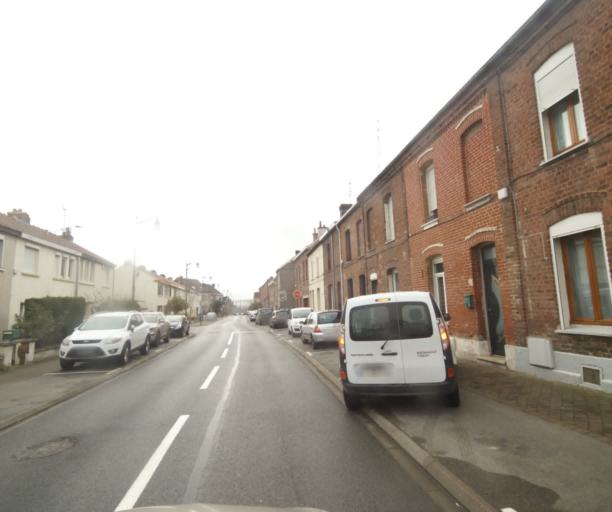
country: FR
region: Nord-Pas-de-Calais
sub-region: Departement du Nord
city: Aulnoy-lez-Valenciennes
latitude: 50.3362
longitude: 3.5274
